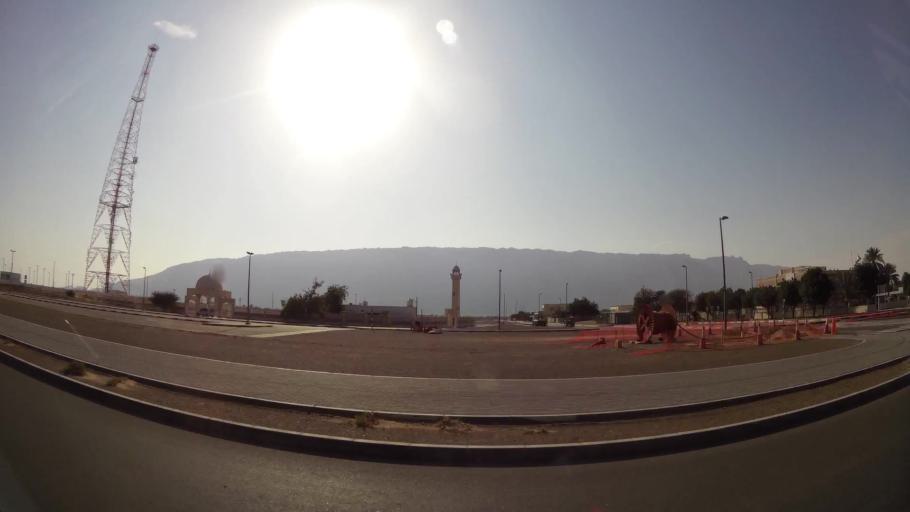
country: AE
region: Abu Dhabi
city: Al Ain
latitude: 24.0320
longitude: 55.8451
